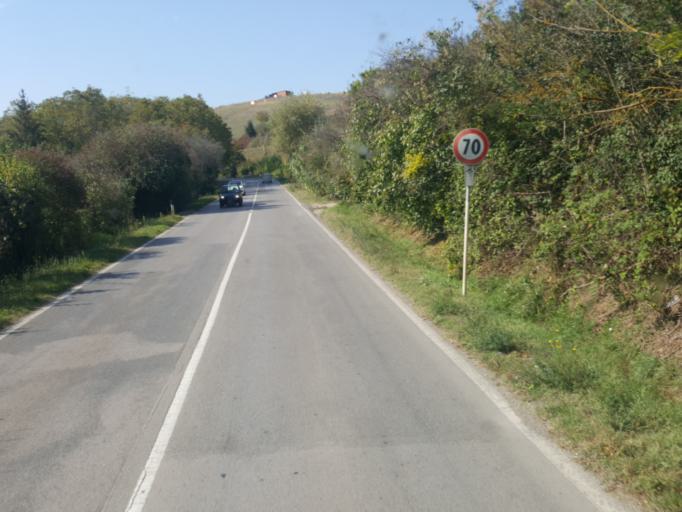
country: IT
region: Tuscany
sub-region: Provincia di Siena
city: Colle di Val d'Elsa
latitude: 43.4130
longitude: 11.1242
